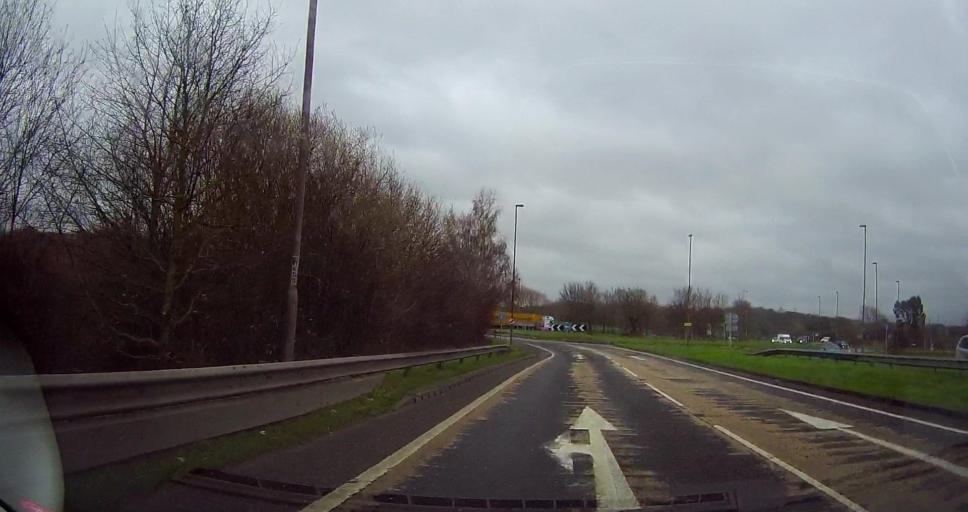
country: GB
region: England
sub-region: Kent
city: Strood
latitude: 51.4151
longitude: 0.5154
